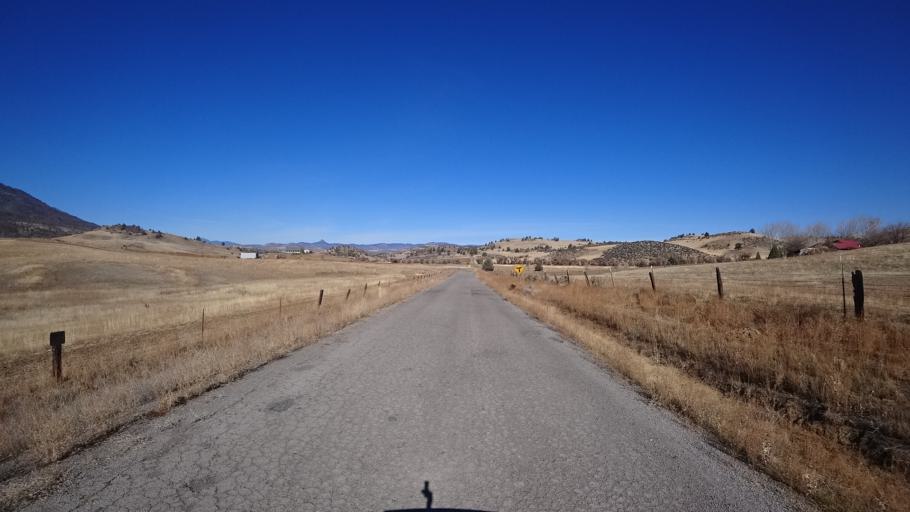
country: US
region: California
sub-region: Siskiyou County
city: Montague
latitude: 41.8461
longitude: -122.4596
